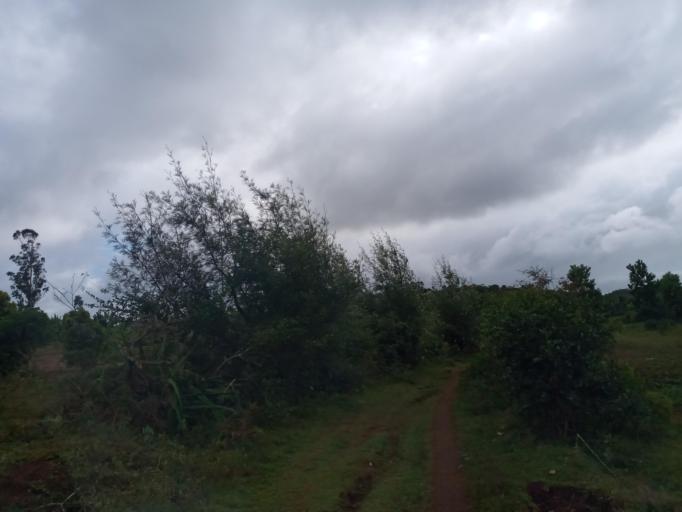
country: MG
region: Atsimo-Atsinanana
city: Vohipaho
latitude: -23.7747
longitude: 47.5357
